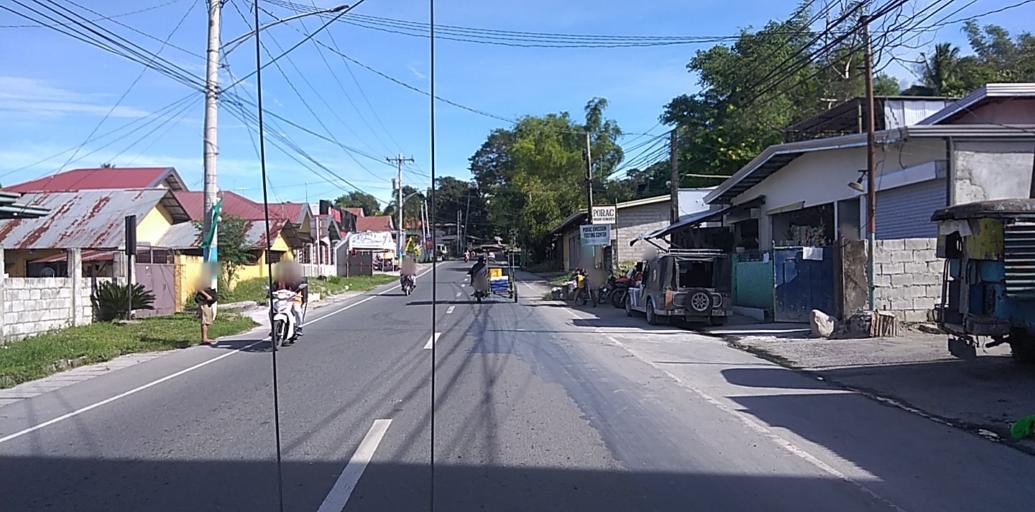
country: PH
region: Central Luzon
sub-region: Province of Pampanga
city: Porac
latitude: 15.0759
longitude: 120.5437
